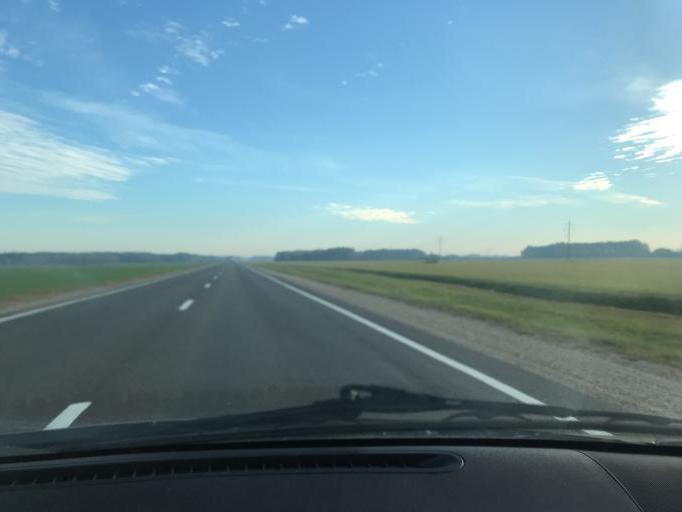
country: BY
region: Brest
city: Drahichyn
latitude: 52.2057
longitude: 25.0622
